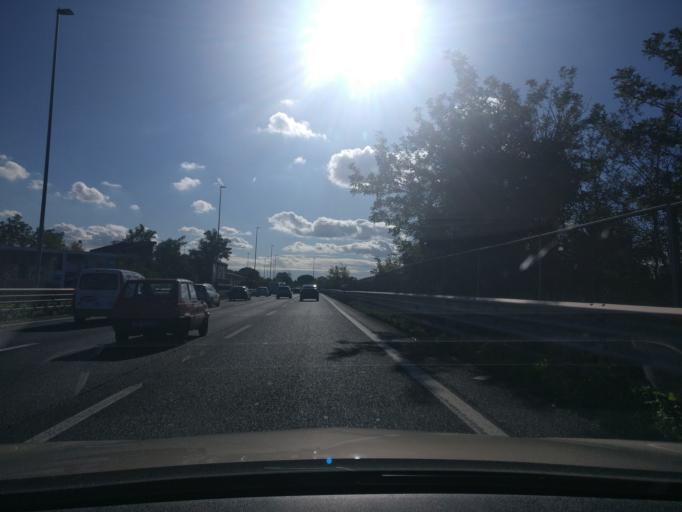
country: IT
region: Latium
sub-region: Citta metropolitana di Roma Capitale
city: Ciampino
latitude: 41.8291
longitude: 12.5822
